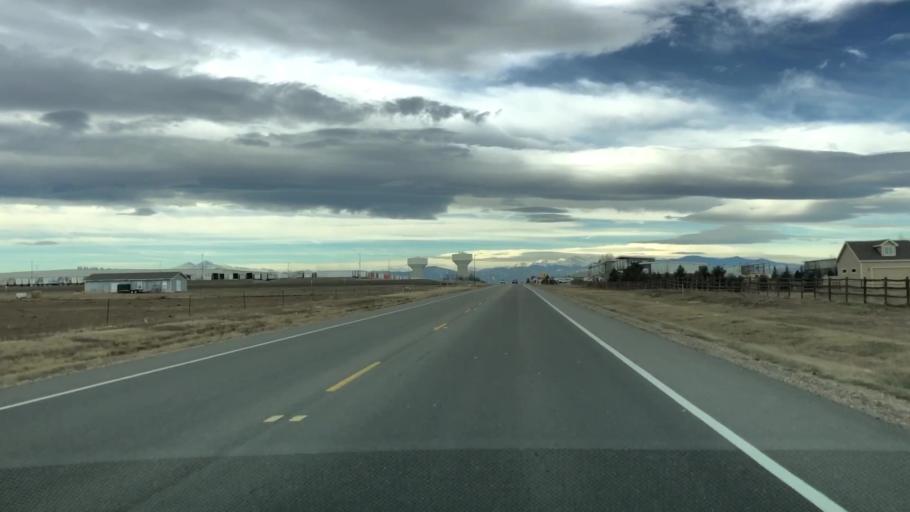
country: US
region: Colorado
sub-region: Weld County
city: Windsor
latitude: 40.4361
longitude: -104.9604
